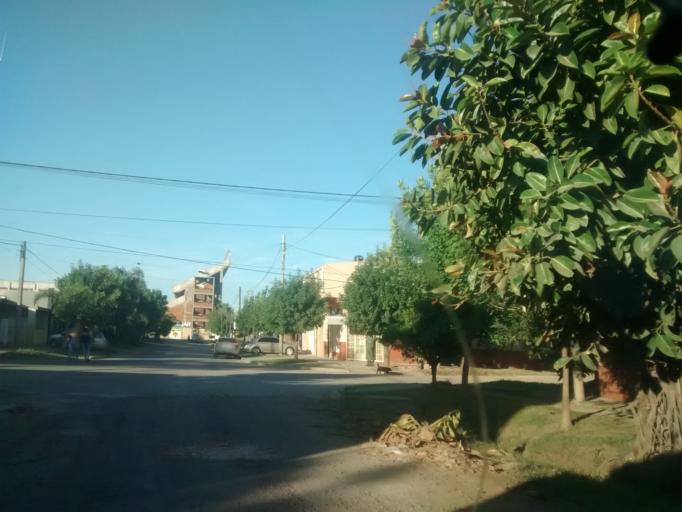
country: AR
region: Chaco
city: Fontana
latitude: -27.4413
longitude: -59.0094
